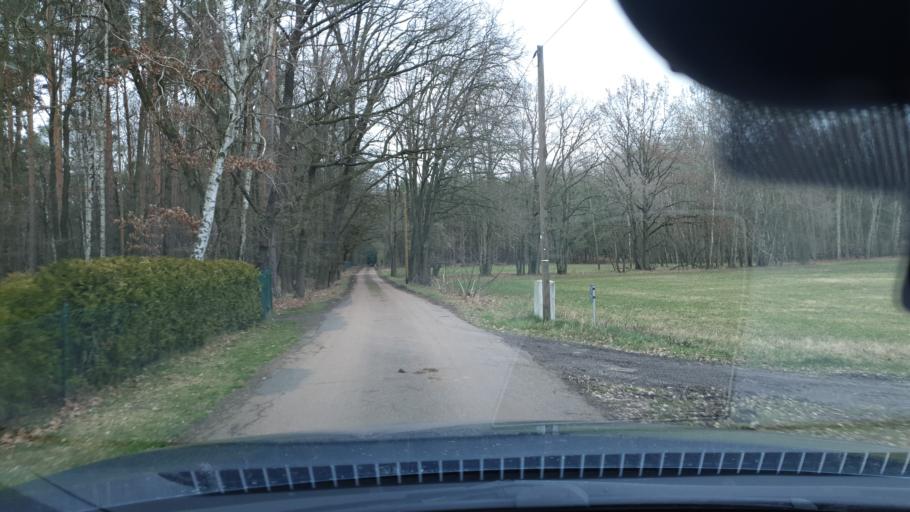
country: DE
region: Saxony-Anhalt
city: Radis
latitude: 51.7481
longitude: 12.5563
